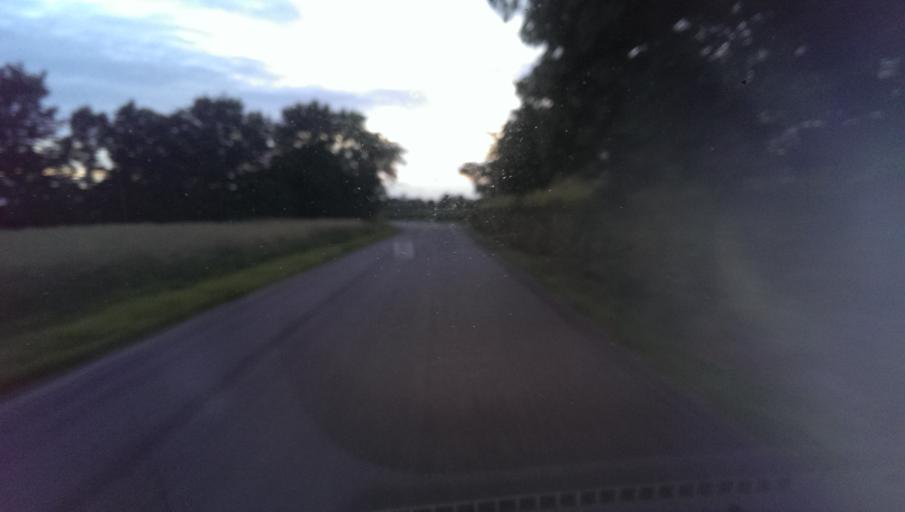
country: DK
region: South Denmark
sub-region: Esbjerg Kommune
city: Esbjerg
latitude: 55.5293
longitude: 8.4893
